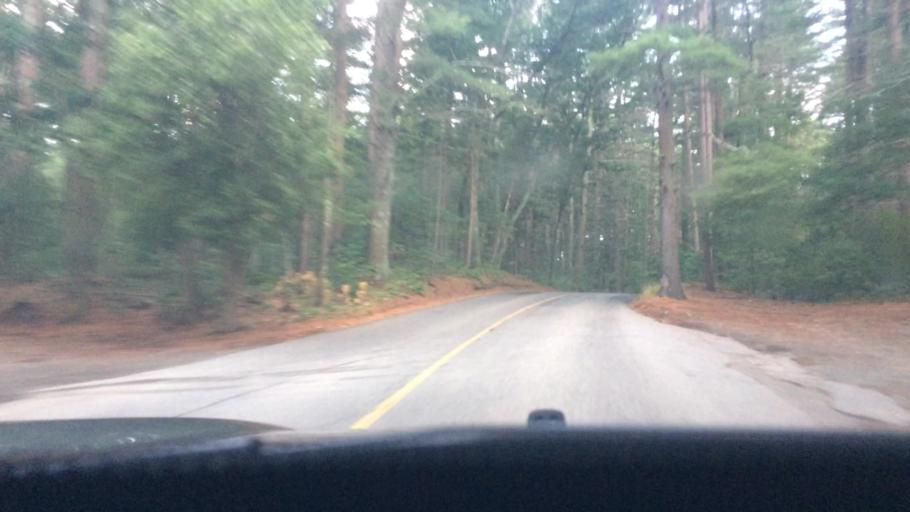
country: US
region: Massachusetts
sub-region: Middlesex County
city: North Reading
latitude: 42.6107
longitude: -71.1078
